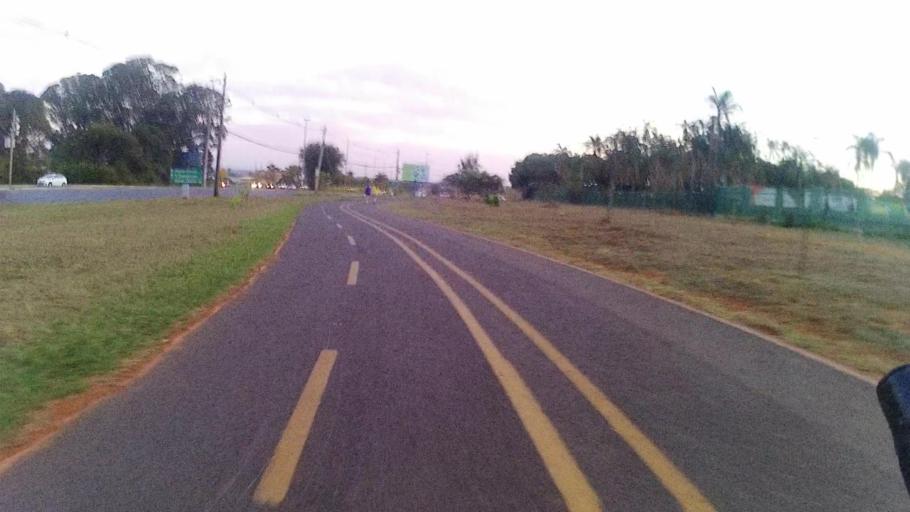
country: BR
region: Federal District
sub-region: Brasilia
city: Brasilia
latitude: -15.8324
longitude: -48.0064
